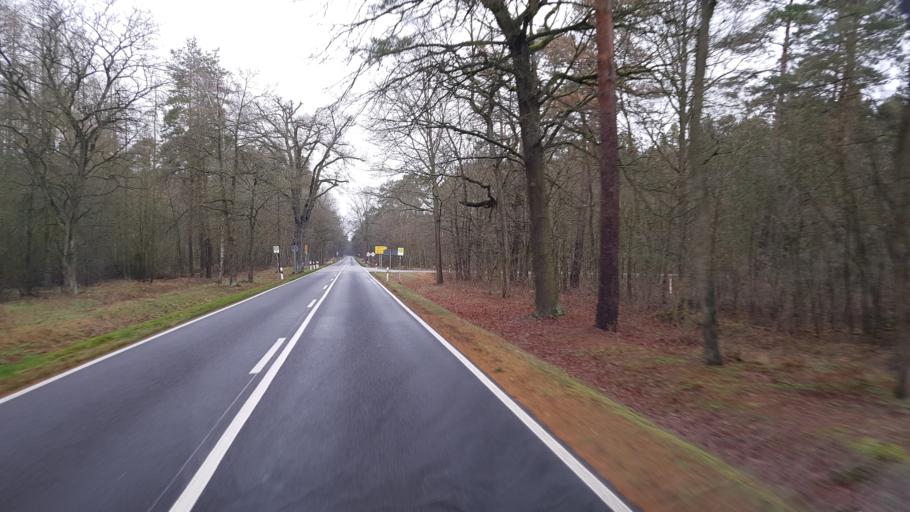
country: DE
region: Brandenburg
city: Altdobern
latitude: 51.7142
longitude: 14.0168
